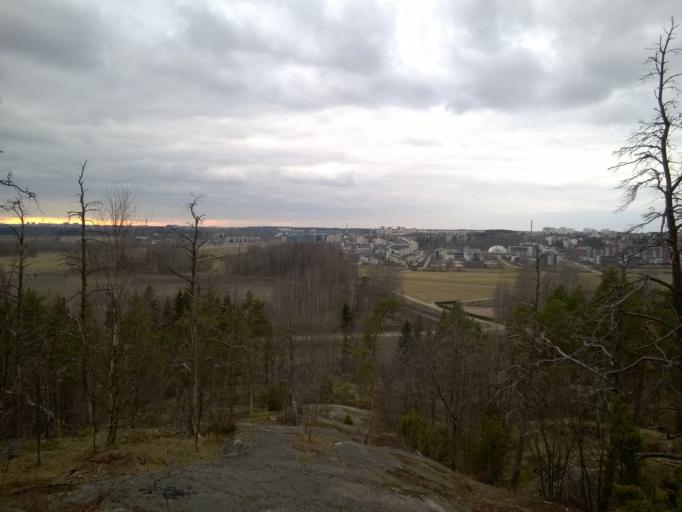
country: FI
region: Uusimaa
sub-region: Helsinki
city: Vantaa
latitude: 60.2260
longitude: 25.0451
